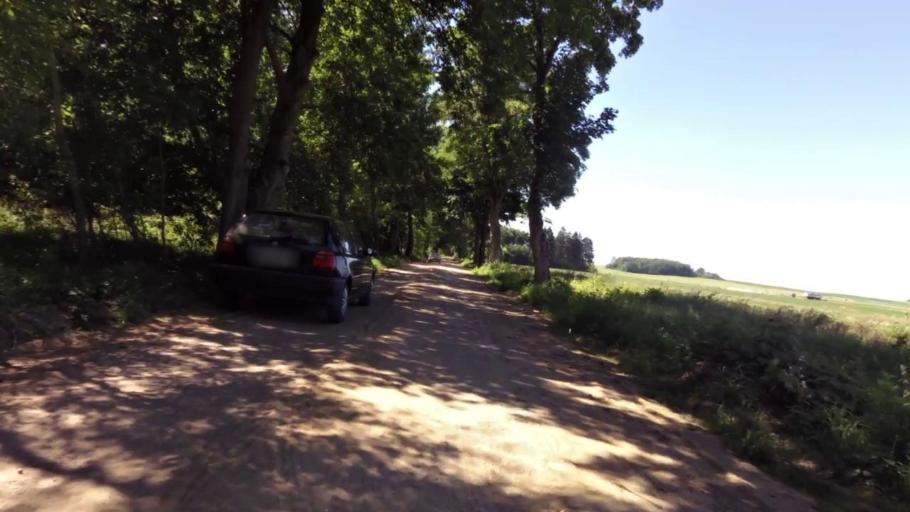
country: PL
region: West Pomeranian Voivodeship
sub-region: Powiat swidwinski
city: Rabino
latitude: 53.8767
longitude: 16.0063
